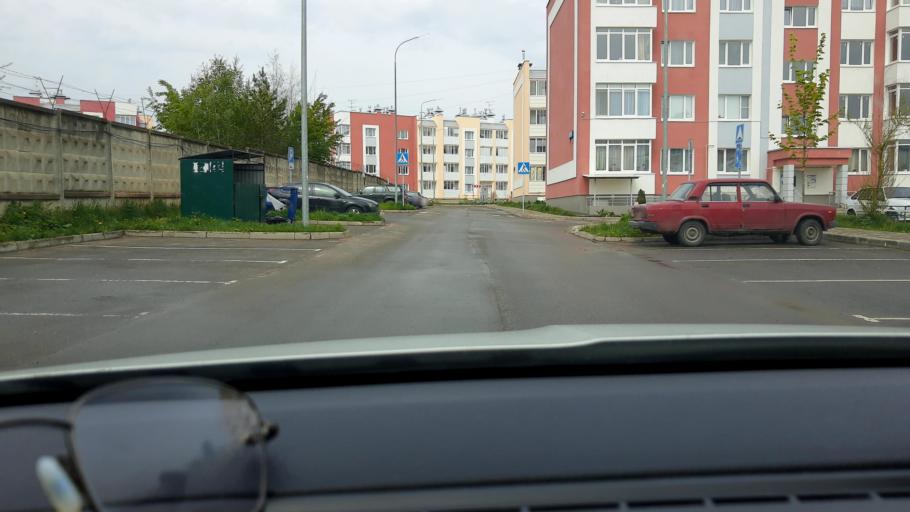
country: RU
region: Moskovskaya
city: Dedovsk
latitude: 55.8391
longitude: 37.1287
